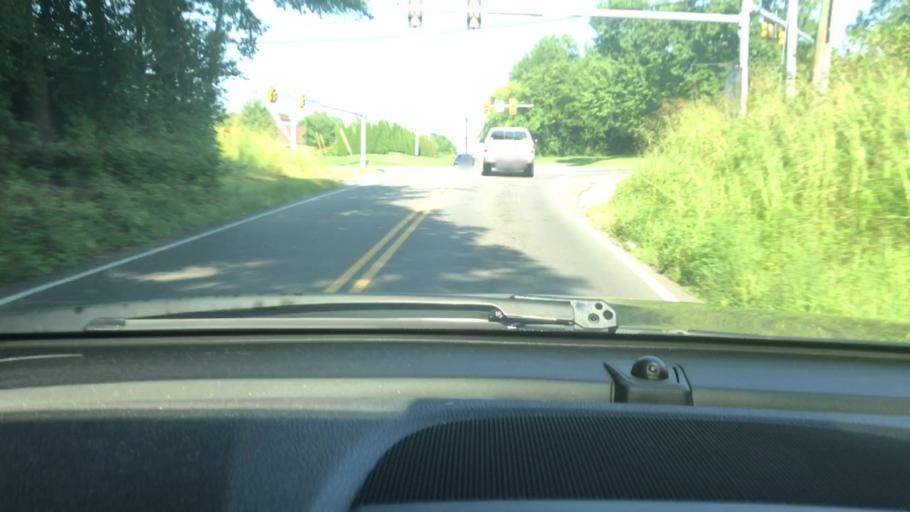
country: US
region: Tennessee
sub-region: Sumner County
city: Shackle Island
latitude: 36.3387
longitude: -86.6143
